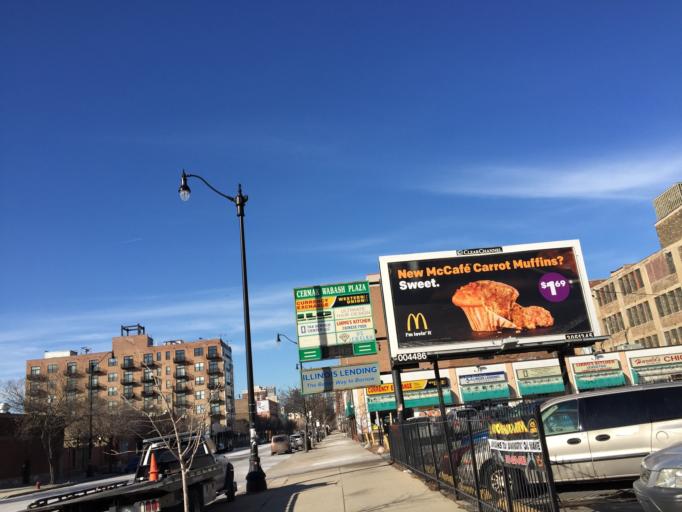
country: US
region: Illinois
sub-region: Cook County
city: Chicago
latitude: 41.8531
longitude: -87.6254
